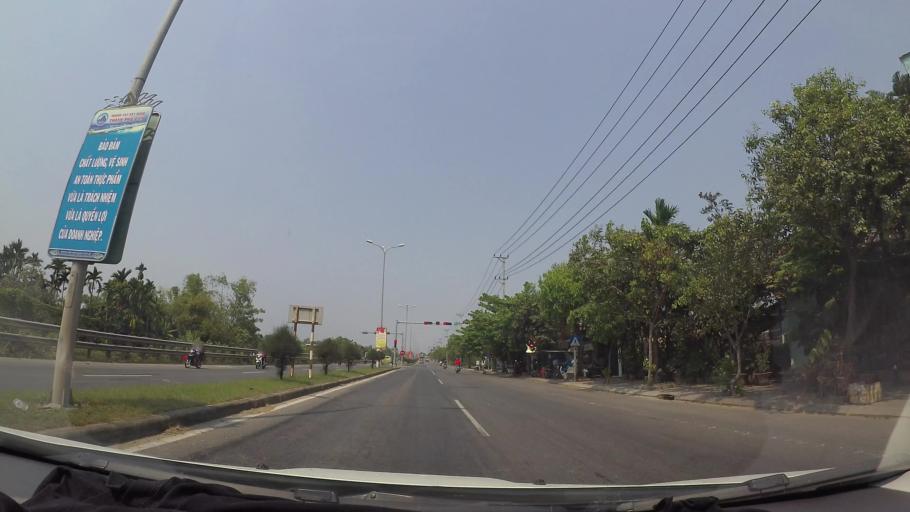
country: VN
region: Da Nang
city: Cam Le
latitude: 16.0055
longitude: 108.1914
